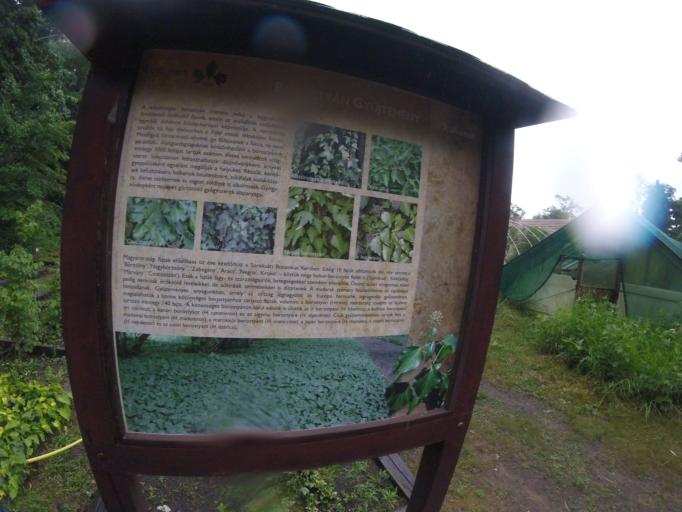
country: HU
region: Budapest
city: Budapest XXIII. keruelet
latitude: 47.4000
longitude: 19.1553
